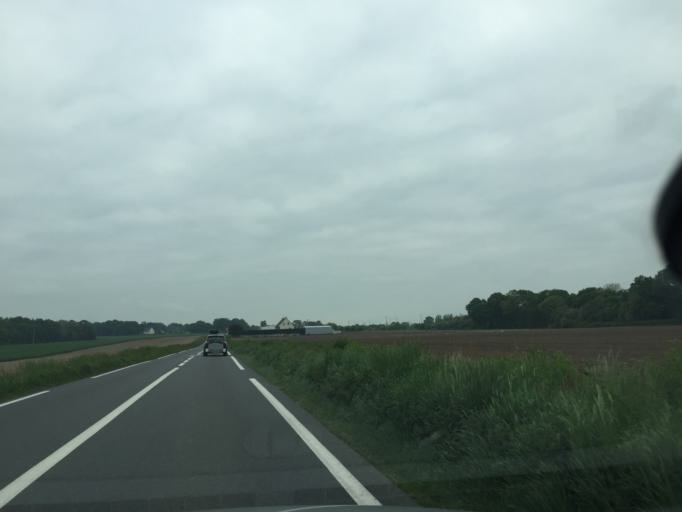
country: FR
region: Brittany
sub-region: Departement des Cotes-d'Armor
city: Henanbihen
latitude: 48.5273
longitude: -2.4243
